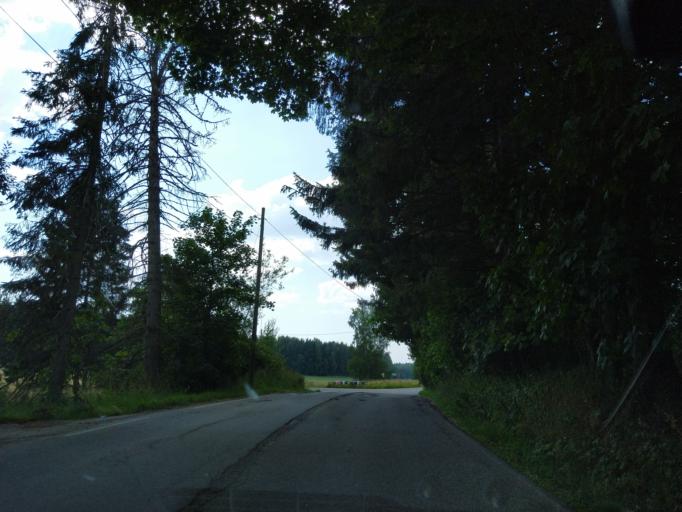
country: FI
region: Uusimaa
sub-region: Helsinki
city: Kirkkonummi
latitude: 60.0534
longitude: 24.4997
